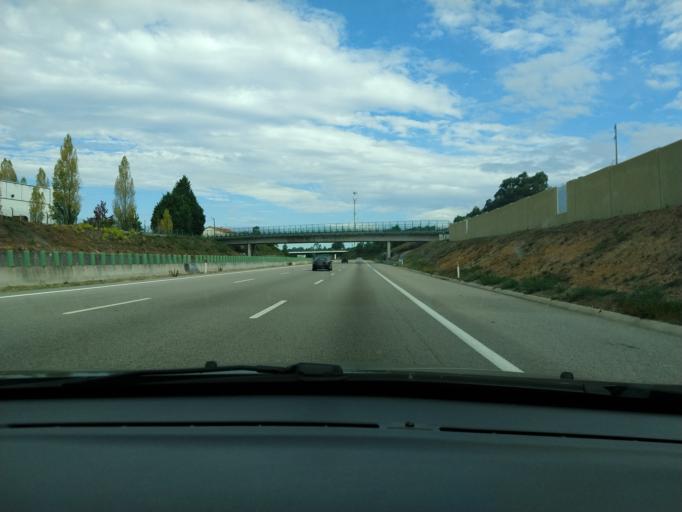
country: PT
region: Aveiro
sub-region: Ovar
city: Valega
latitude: 40.8772
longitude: -8.5604
